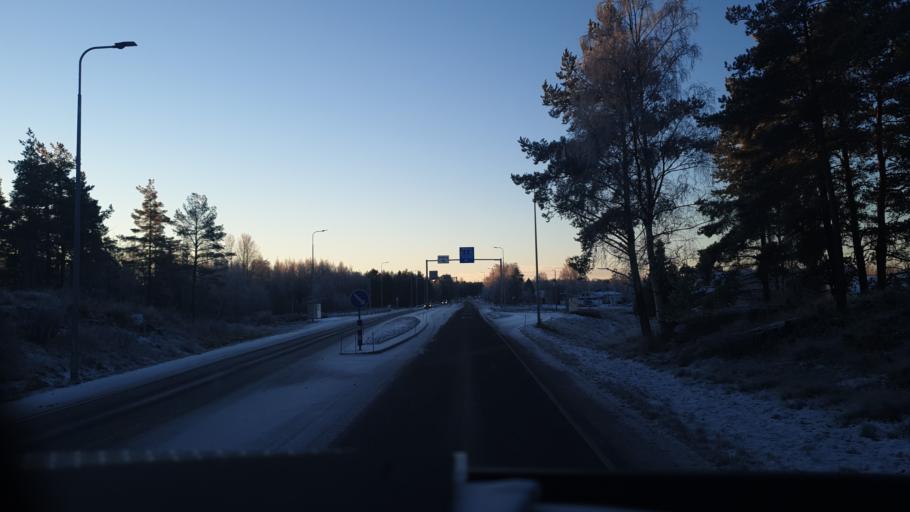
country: FI
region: Northern Ostrobothnia
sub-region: Raahe
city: Pyhaejoki
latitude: 64.4662
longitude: 24.2629
